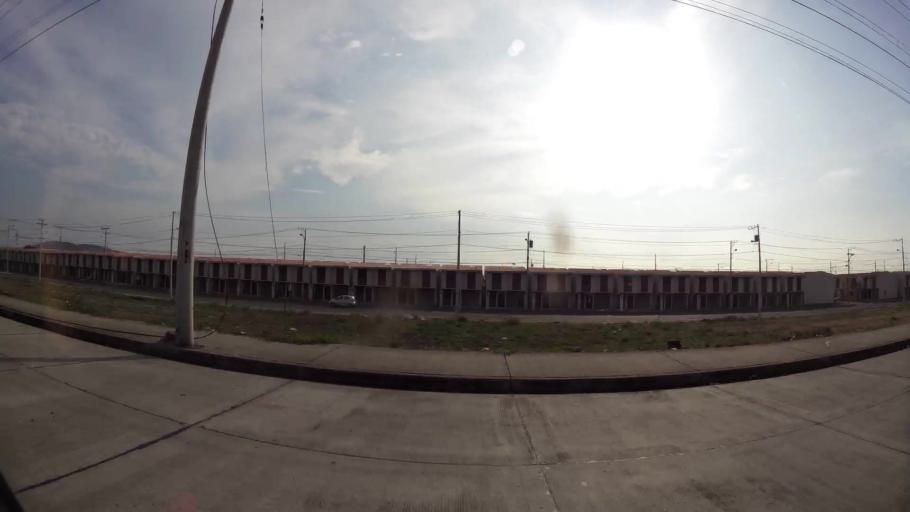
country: EC
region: Guayas
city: Eloy Alfaro
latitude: -2.0674
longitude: -79.9000
